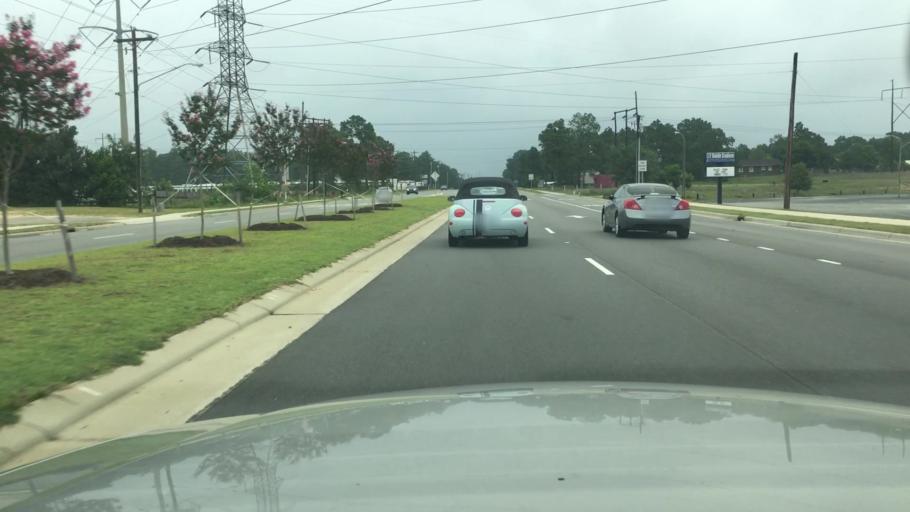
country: US
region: North Carolina
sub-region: Cumberland County
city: Hope Mills
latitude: 35.0081
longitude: -78.9123
